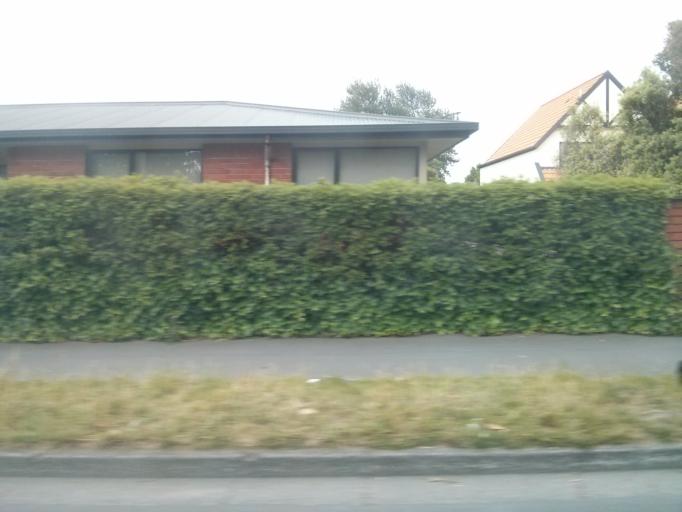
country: NZ
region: Canterbury
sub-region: Christchurch City
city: Christchurch
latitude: -43.5309
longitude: 172.5838
